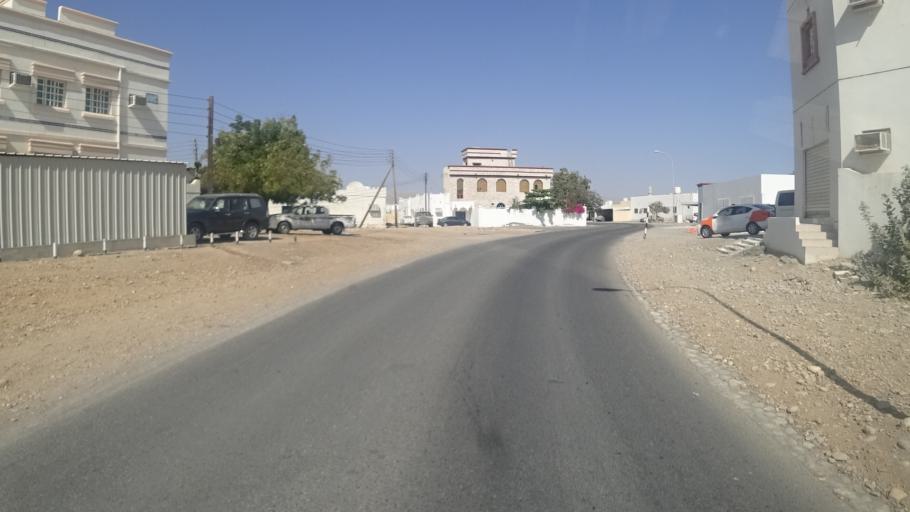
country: OM
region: Ash Sharqiyah
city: Sur
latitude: 22.5401
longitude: 59.4856
